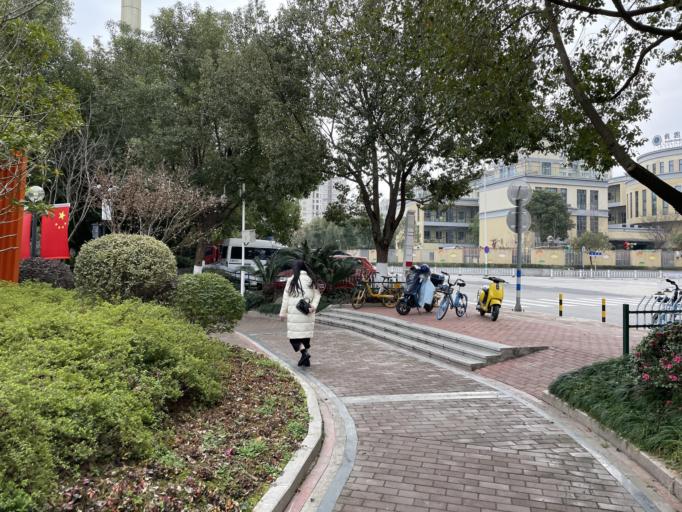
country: CN
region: Zhejiang Sheng
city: Wenzhou
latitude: 27.9948
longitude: 120.6655
